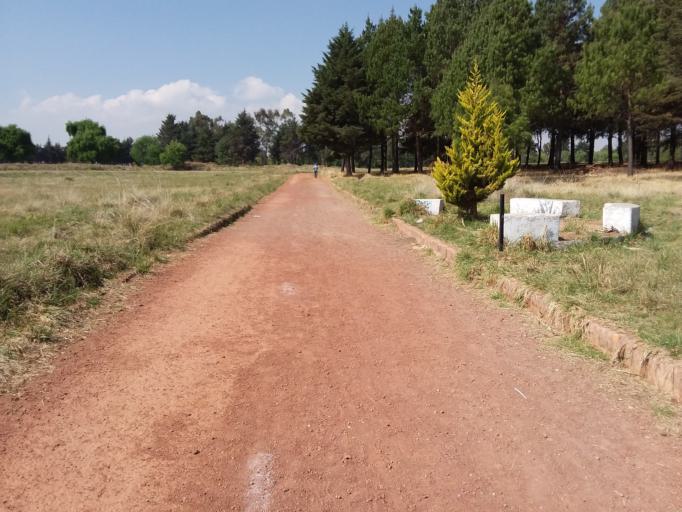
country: MX
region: Mexico
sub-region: Toluca
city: San Antonio Buenavista
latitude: 19.2739
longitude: -99.6948
